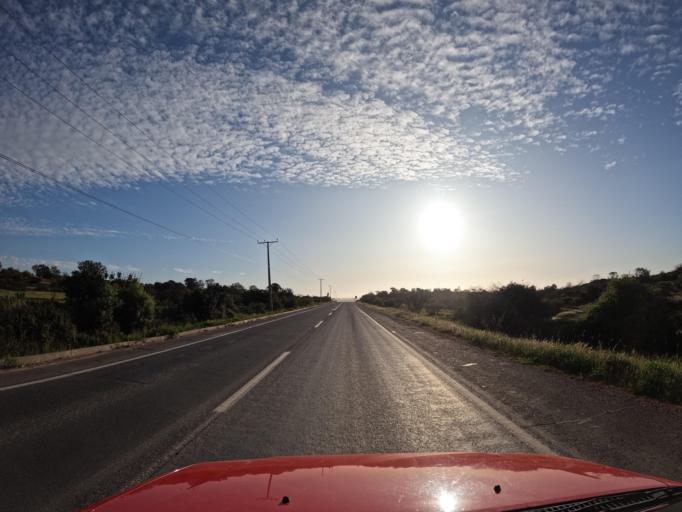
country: CL
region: Valparaiso
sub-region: San Antonio Province
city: San Antonio
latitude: -34.0866
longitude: -71.6737
